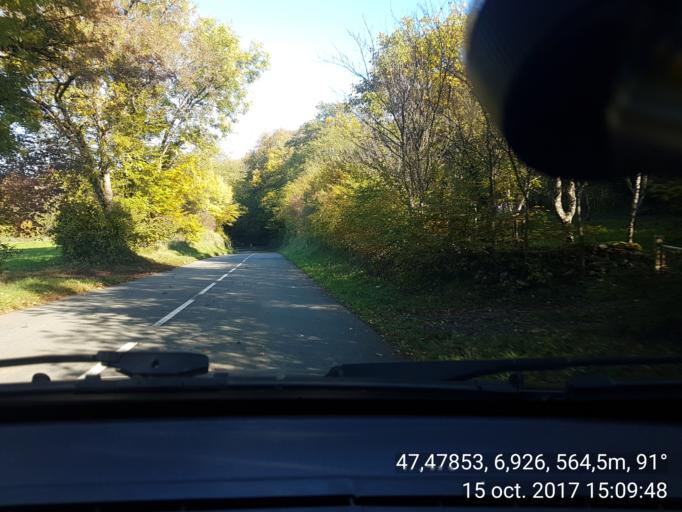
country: FR
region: Franche-Comte
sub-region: Territoire de Belfort
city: Beaucourt
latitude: 47.4786
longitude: 6.9258
